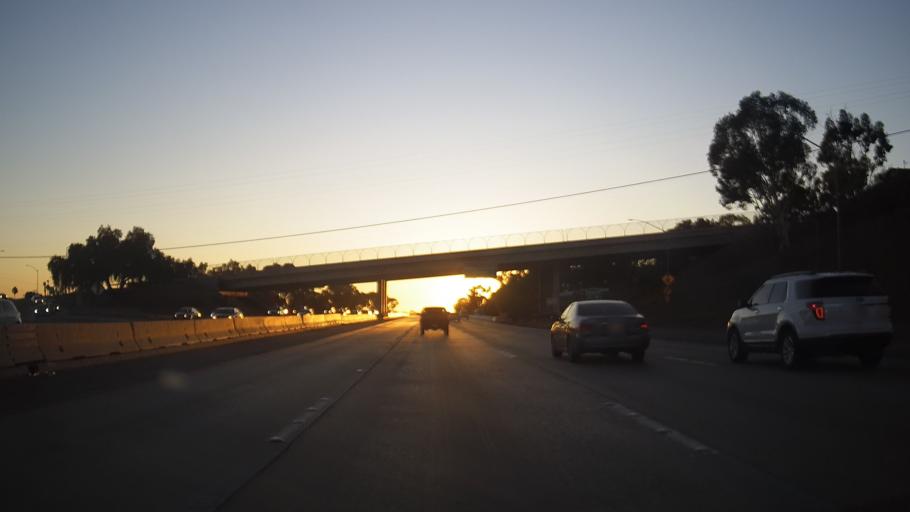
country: US
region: California
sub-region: San Diego County
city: Lemon Grove
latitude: 32.7464
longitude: -117.0299
